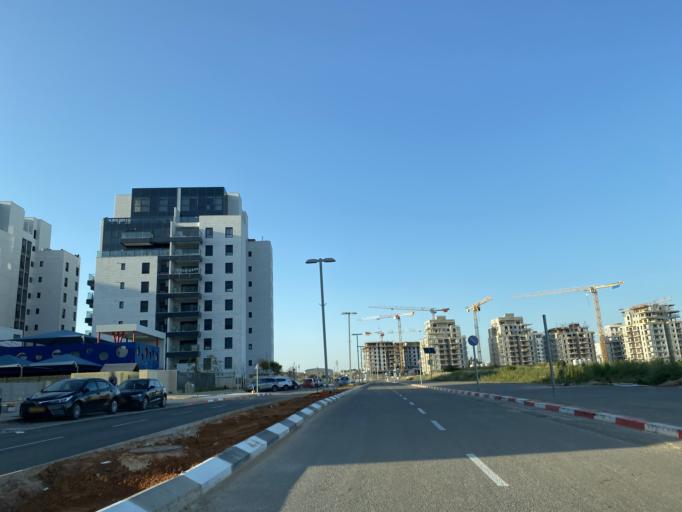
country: IL
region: Tel Aviv
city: Herzliyya
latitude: 32.1582
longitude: 34.8229
